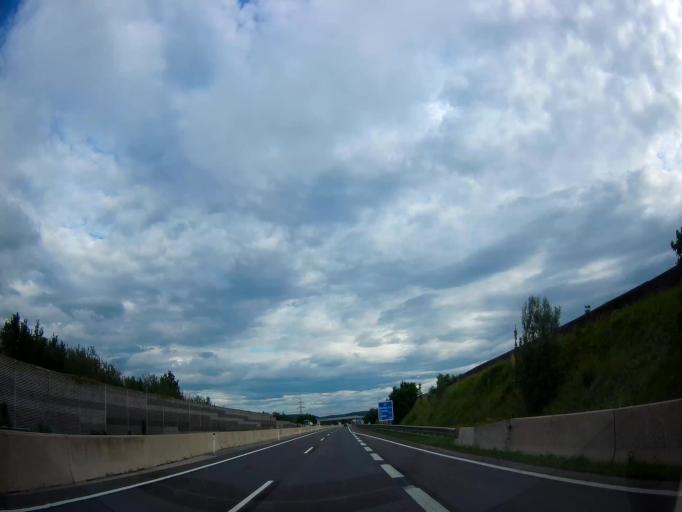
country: AT
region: Lower Austria
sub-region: Politischer Bezirk Sankt Polten
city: Traismauer
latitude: 48.3648
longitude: 15.7188
